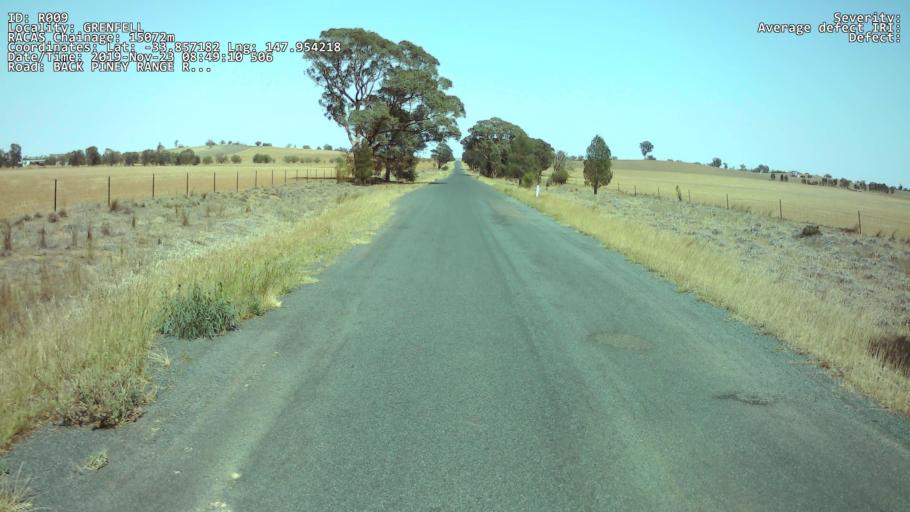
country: AU
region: New South Wales
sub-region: Weddin
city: Grenfell
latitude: -33.8572
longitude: 147.9542
